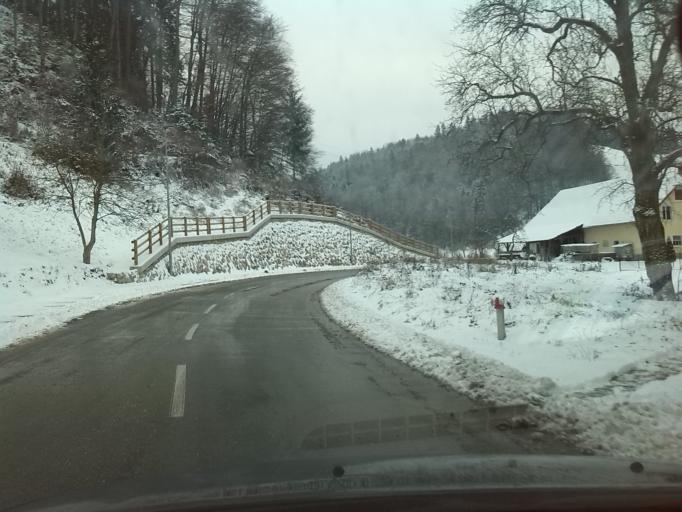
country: SI
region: Lukovica
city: Lukovica pri Domzalah
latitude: 46.2198
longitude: 14.6980
